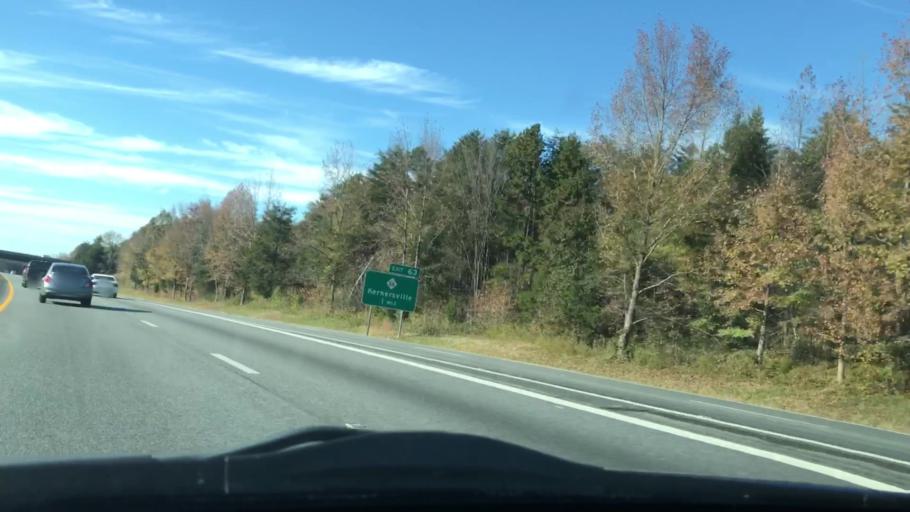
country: US
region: North Carolina
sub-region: Guilford County
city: High Point
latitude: 36.0156
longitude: -80.0395
